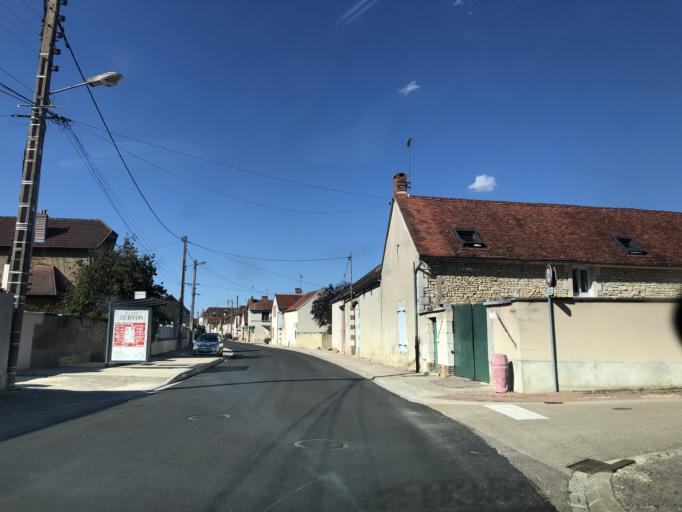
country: FR
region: Bourgogne
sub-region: Departement de l'Yonne
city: Appoigny
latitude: 47.8734
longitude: 3.5267
